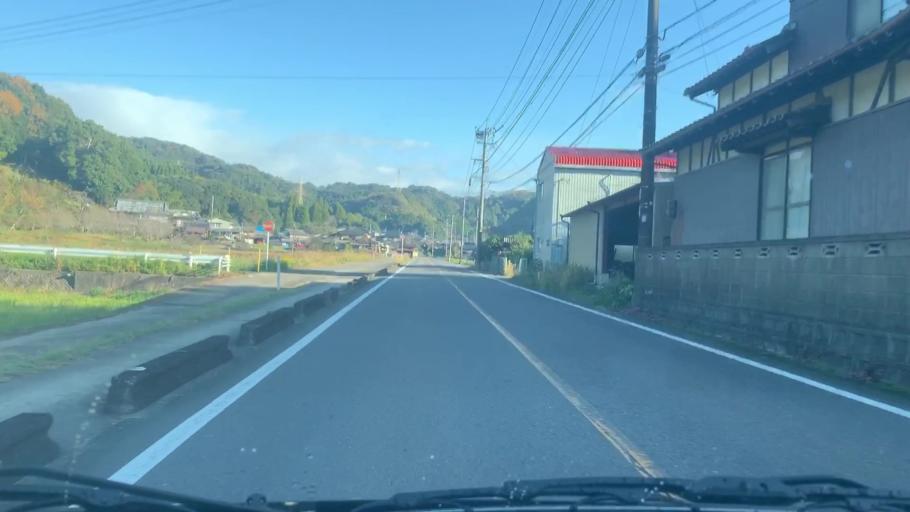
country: JP
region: Saga Prefecture
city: Takeocho-takeo
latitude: 33.2294
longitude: 130.0597
